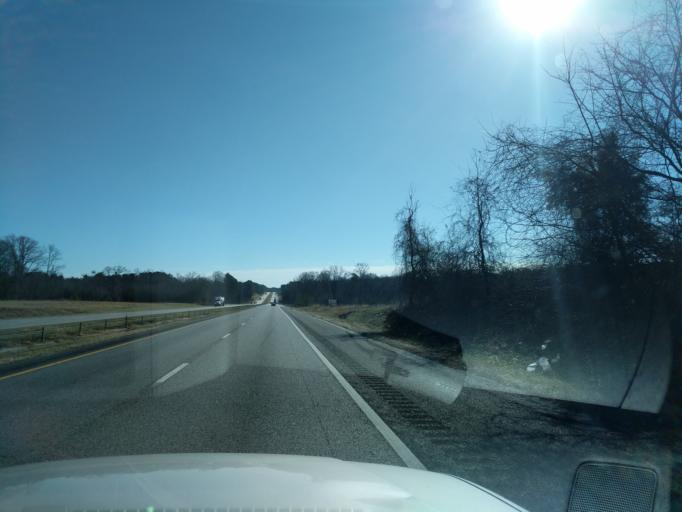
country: US
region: South Carolina
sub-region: Spartanburg County
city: Woodruff
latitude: 34.6165
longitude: -82.0831
